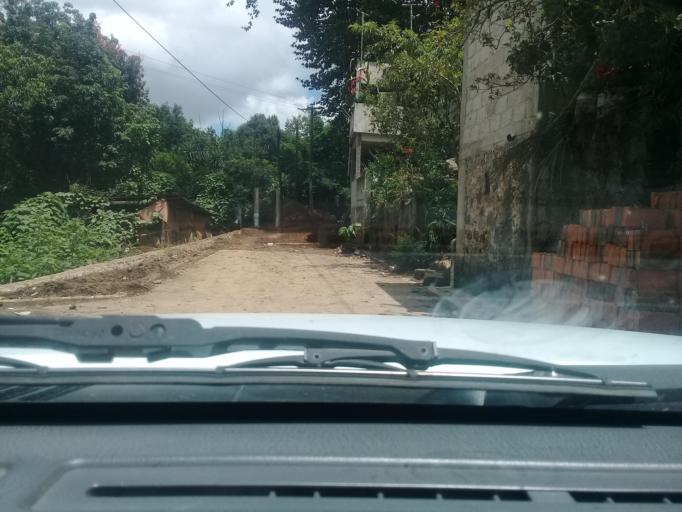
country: MX
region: Veracruz
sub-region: Tlalnelhuayocan
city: Otilpan
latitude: 19.5368
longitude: -96.9717
